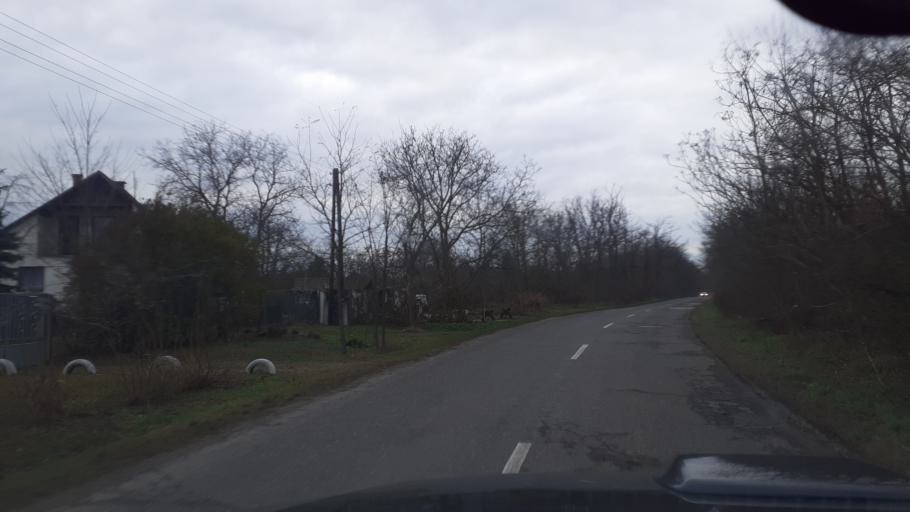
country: HU
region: Bacs-Kiskun
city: Szalkszentmarton
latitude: 46.9329
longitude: 19.0927
